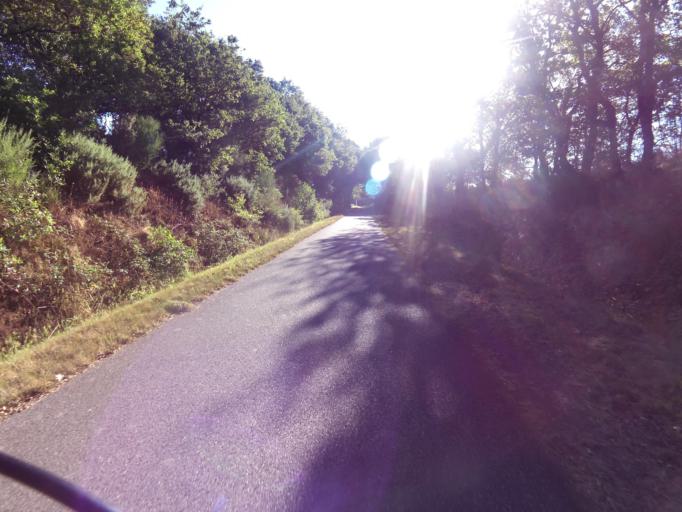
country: FR
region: Brittany
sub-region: Departement du Morbihan
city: Ploermel
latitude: 47.9237
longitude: -2.4157
